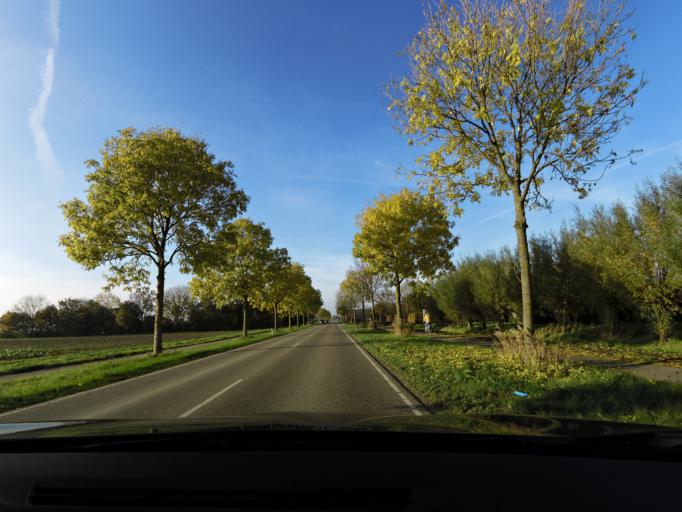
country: NL
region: North Brabant
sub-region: Gemeente Moerdijk
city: Klundert
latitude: 51.6337
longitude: 4.6229
